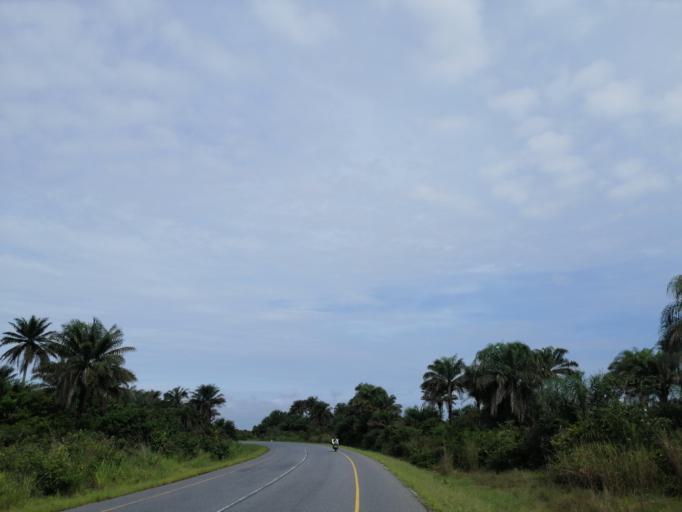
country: SL
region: Northern Province
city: Port Loko
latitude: 8.7702
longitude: -12.8803
